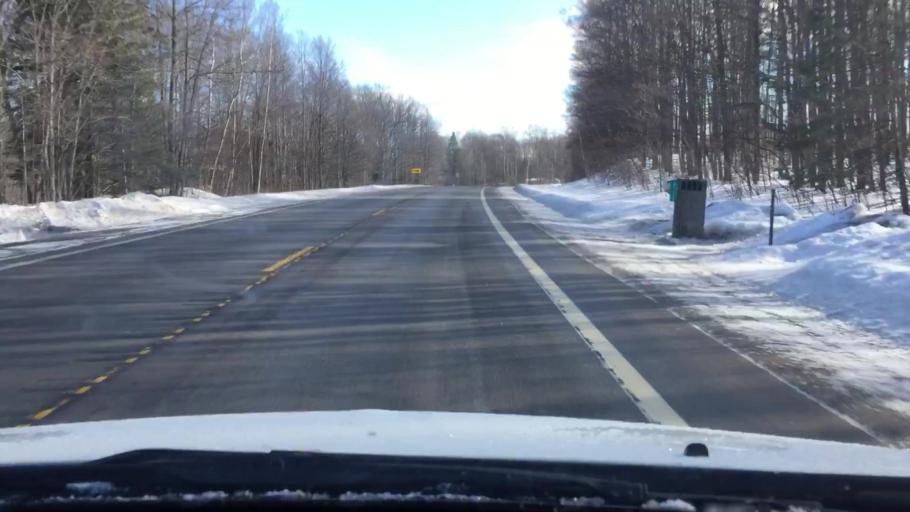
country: US
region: Michigan
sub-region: Antrim County
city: Mancelona
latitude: 44.9873
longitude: -85.0572
